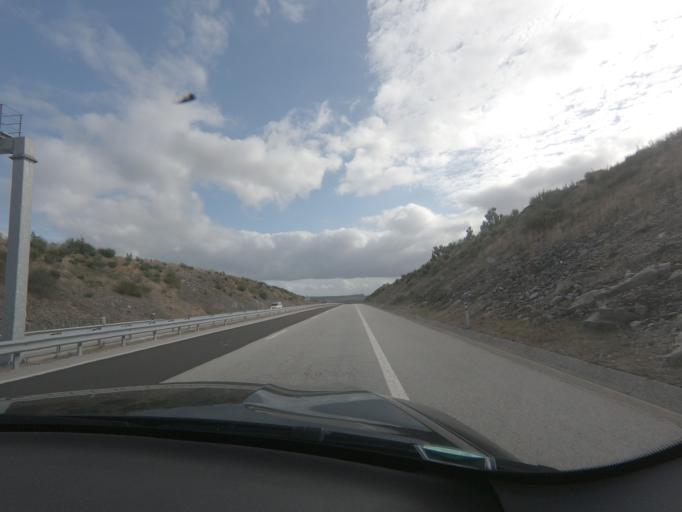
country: PT
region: Viseu
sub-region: Castro Daire
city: Castro Daire
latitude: 40.9788
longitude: -7.8841
